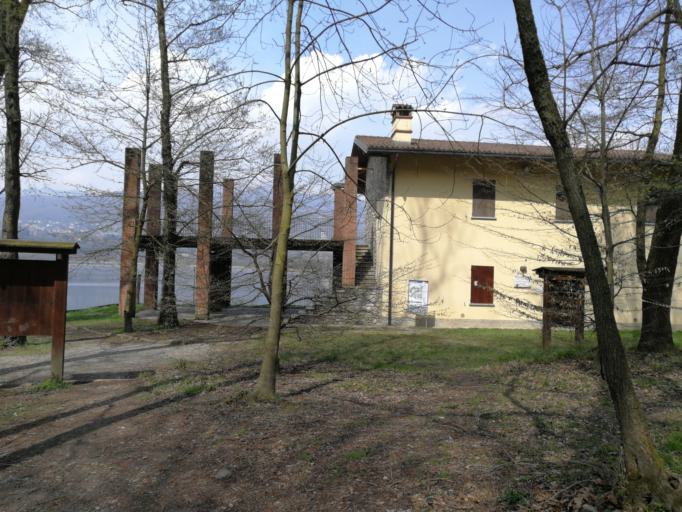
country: IT
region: Lombardy
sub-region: Provincia di Como
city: Nobile-Monguzzo
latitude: 45.7862
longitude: 9.2237
